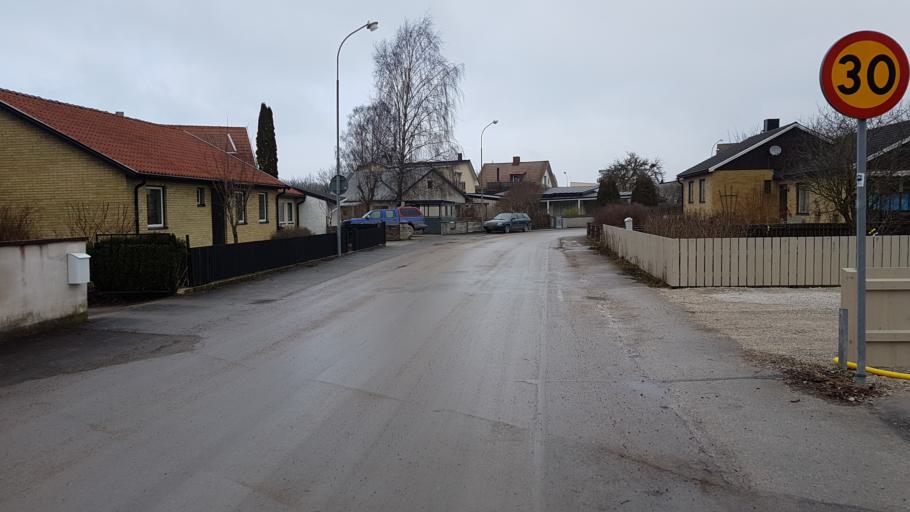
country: SE
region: Gotland
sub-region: Gotland
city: Visby
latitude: 57.6352
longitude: 18.3100
